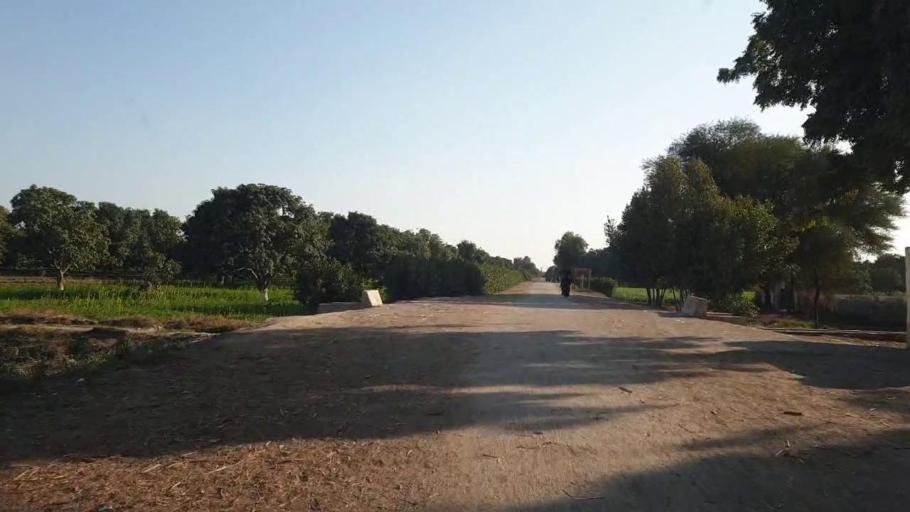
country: PK
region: Sindh
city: Tando Allahyar
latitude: 25.3672
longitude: 68.6825
